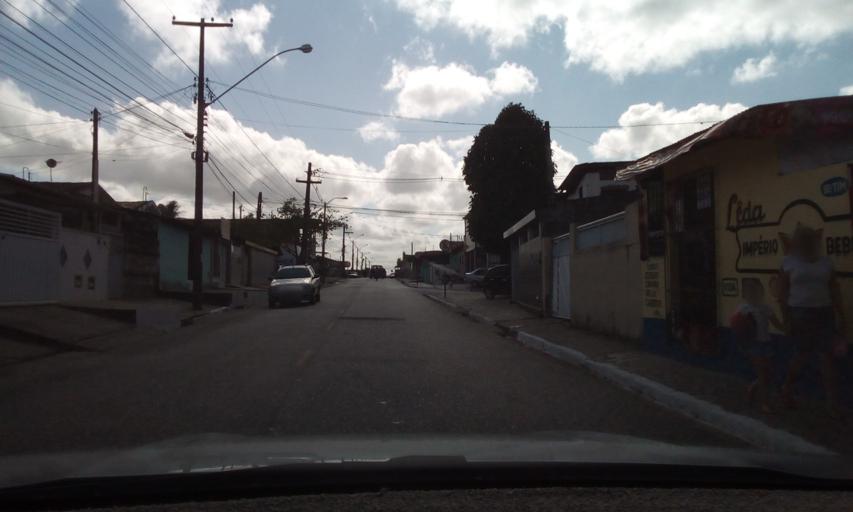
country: BR
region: Paraiba
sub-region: Bayeux
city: Bayeux
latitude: -7.1552
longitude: -34.9002
